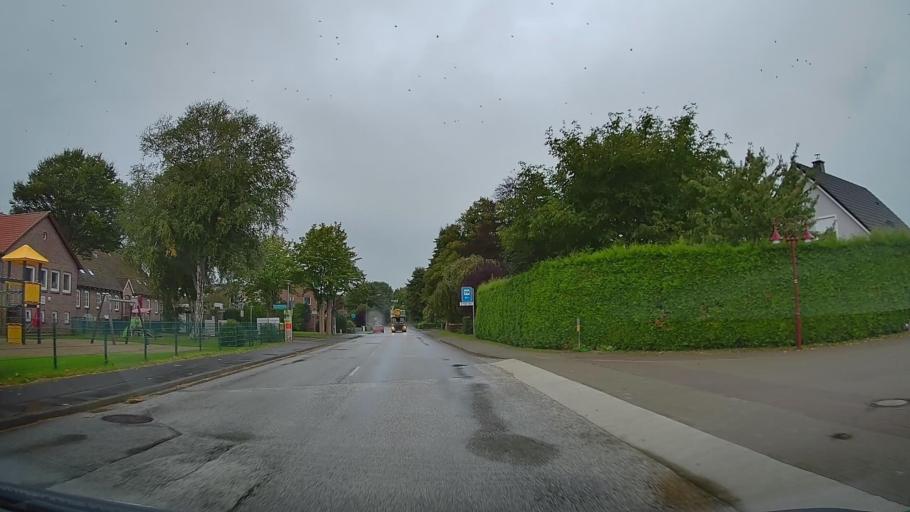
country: DE
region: Schleswig-Holstein
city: Brokdorf
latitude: 53.8651
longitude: 9.3181
